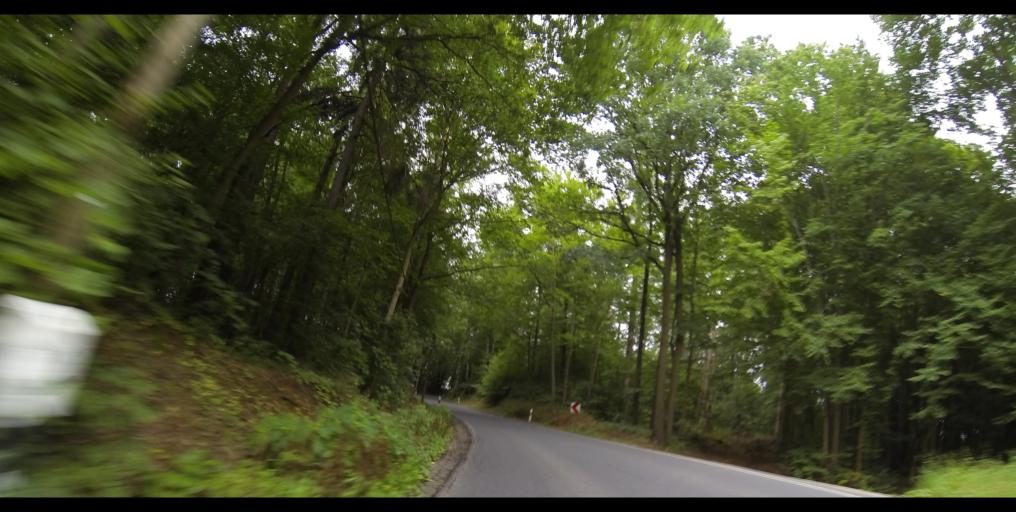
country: DE
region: Saxony
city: Reinsberg
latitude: 51.0202
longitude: 13.3465
